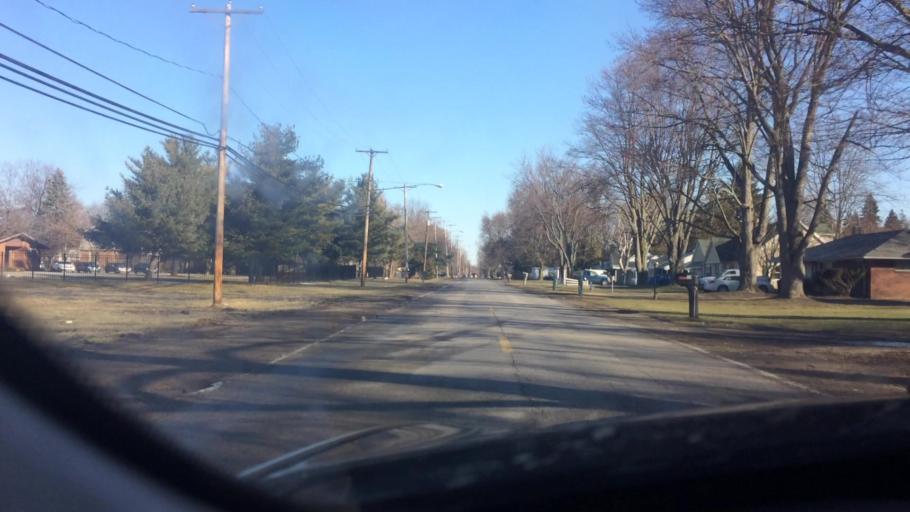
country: US
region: Ohio
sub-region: Lucas County
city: Ottawa Hills
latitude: 41.6397
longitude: -83.6406
